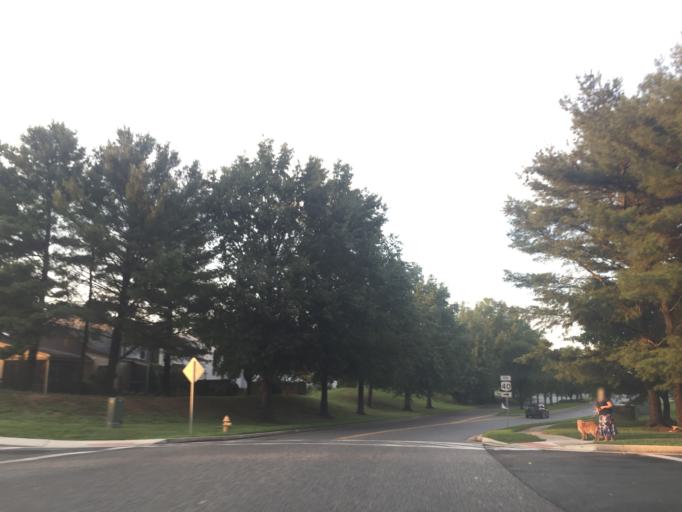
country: US
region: Maryland
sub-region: Harford County
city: Riverside
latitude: 39.4749
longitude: -76.2401
